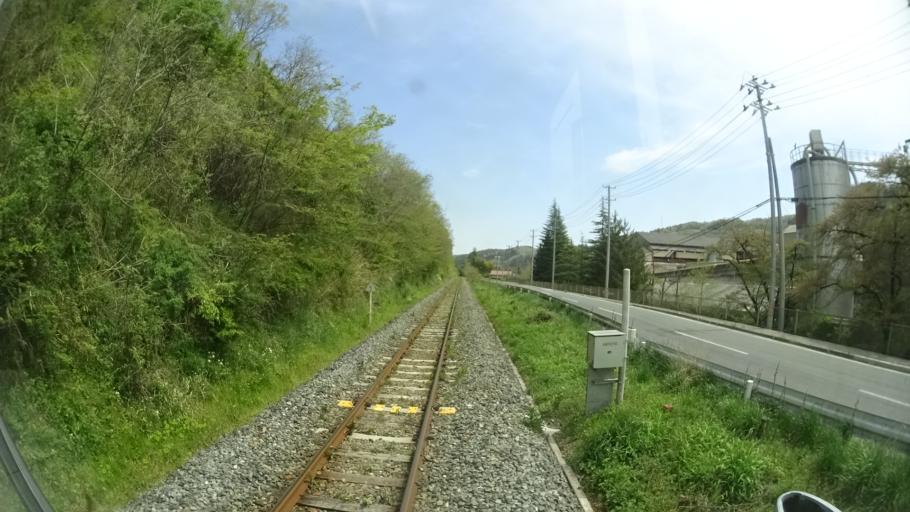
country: JP
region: Iwate
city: Ichinoseki
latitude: 38.9847
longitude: 141.2441
